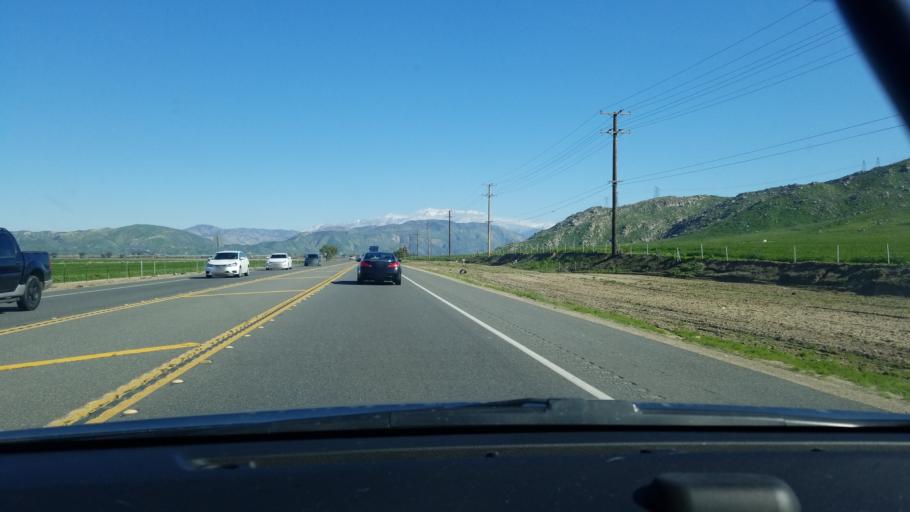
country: US
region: California
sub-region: Riverside County
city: Lakeview
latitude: 33.8400
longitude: -117.0836
